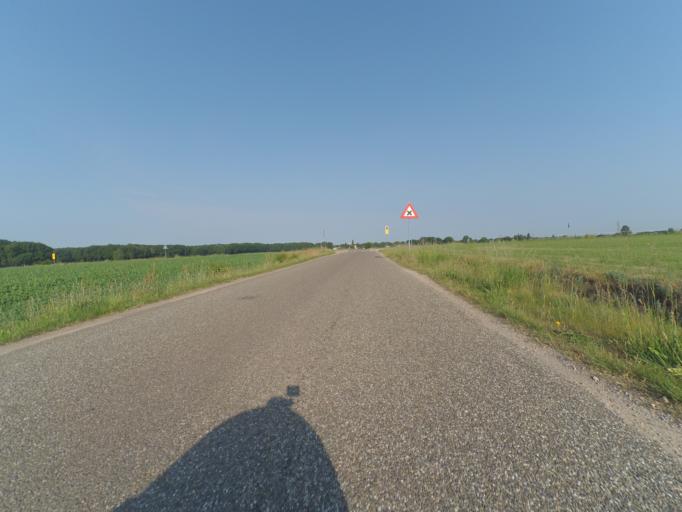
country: NL
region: Gelderland
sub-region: Gemeente Apeldoorn
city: Beekbergen
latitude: 52.1563
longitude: 5.9859
